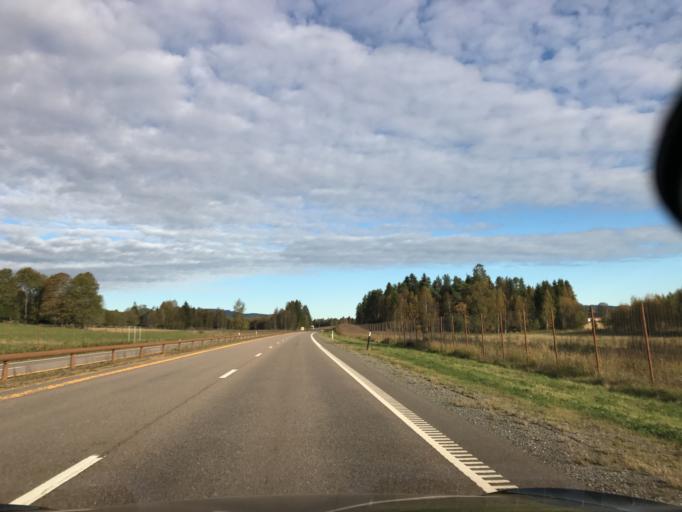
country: NO
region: Akershus
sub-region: Eidsvoll
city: Eidsvoll
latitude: 60.3624
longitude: 11.2043
